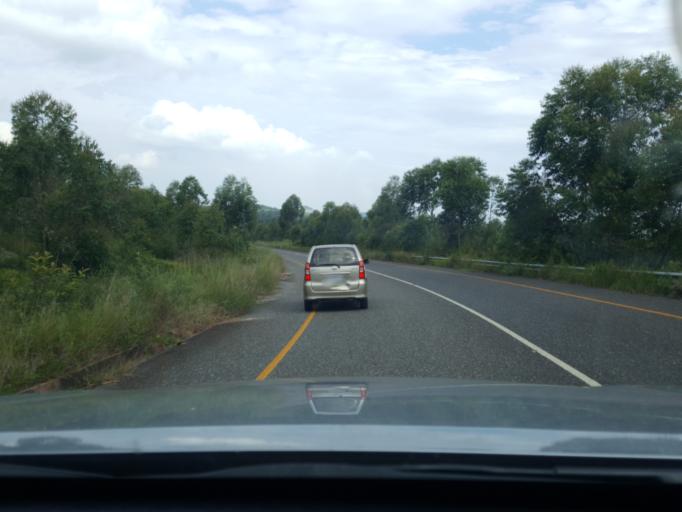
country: ZA
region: Mpumalanga
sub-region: Ehlanzeni District
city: White River
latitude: -25.1771
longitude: 30.8741
